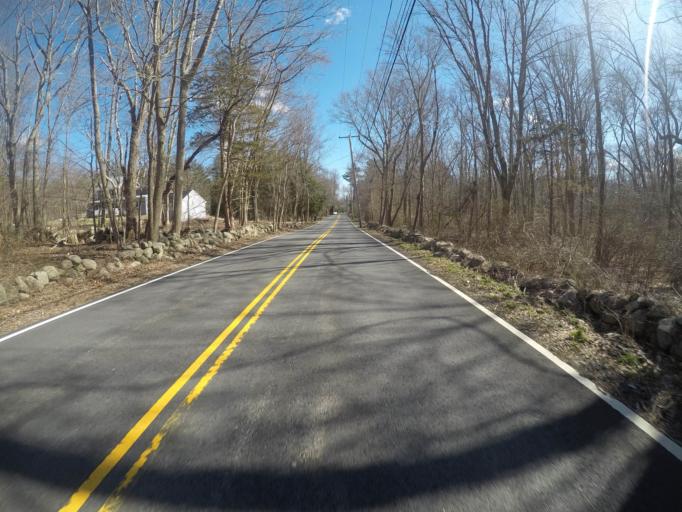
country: US
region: Massachusetts
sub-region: Bristol County
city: Easton
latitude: 42.0430
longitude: -71.1410
